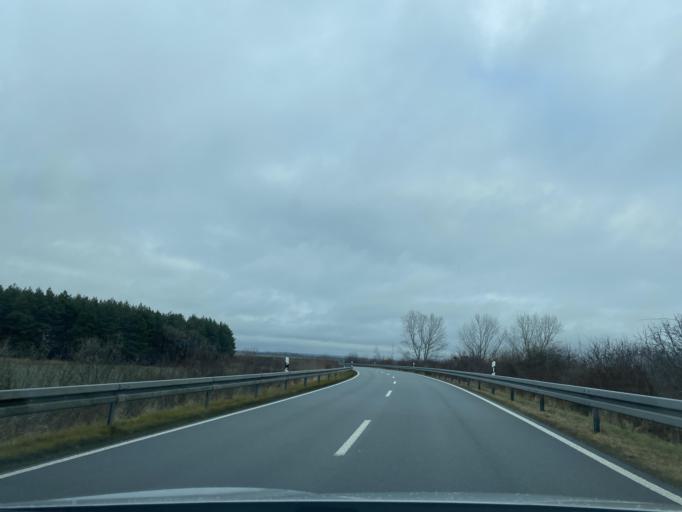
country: DE
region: Saxony
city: Goerlitz
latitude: 51.2278
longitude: 14.9713
